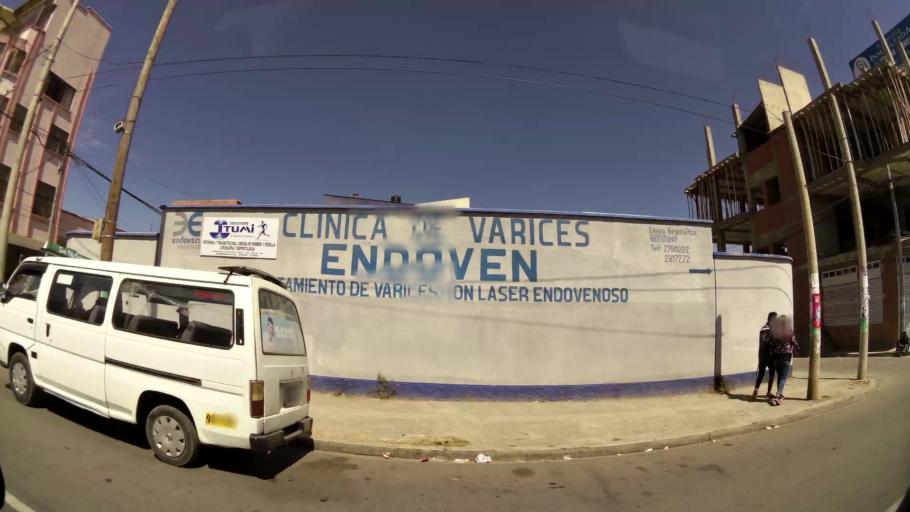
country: BO
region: La Paz
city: La Paz
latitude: -16.5277
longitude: -68.1489
